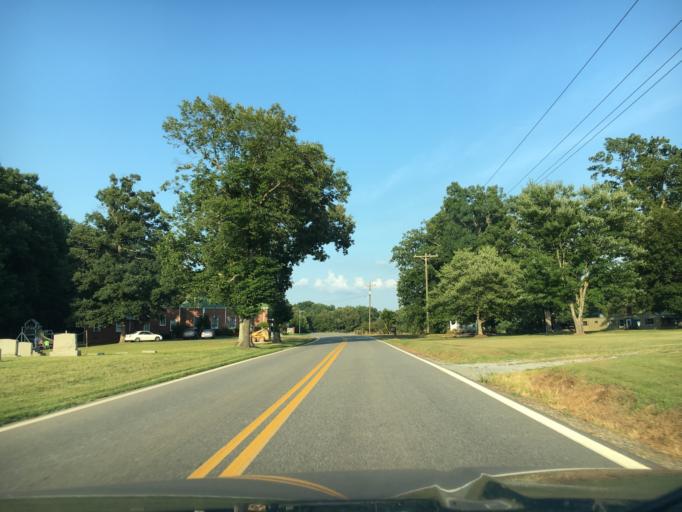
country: US
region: Virginia
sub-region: Halifax County
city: Mountain Road
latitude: 36.8330
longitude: -79.1427
